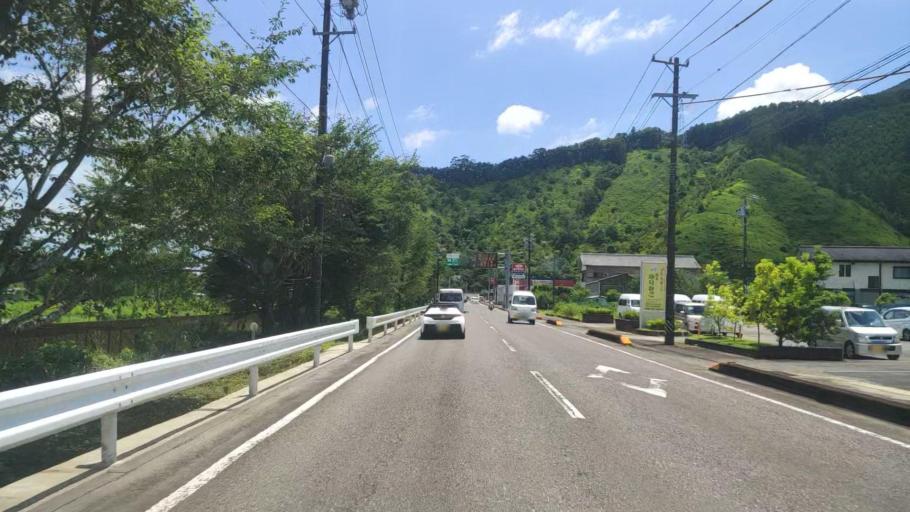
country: JP
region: Mie
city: Owase
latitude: 34.1245
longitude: 136.2164
